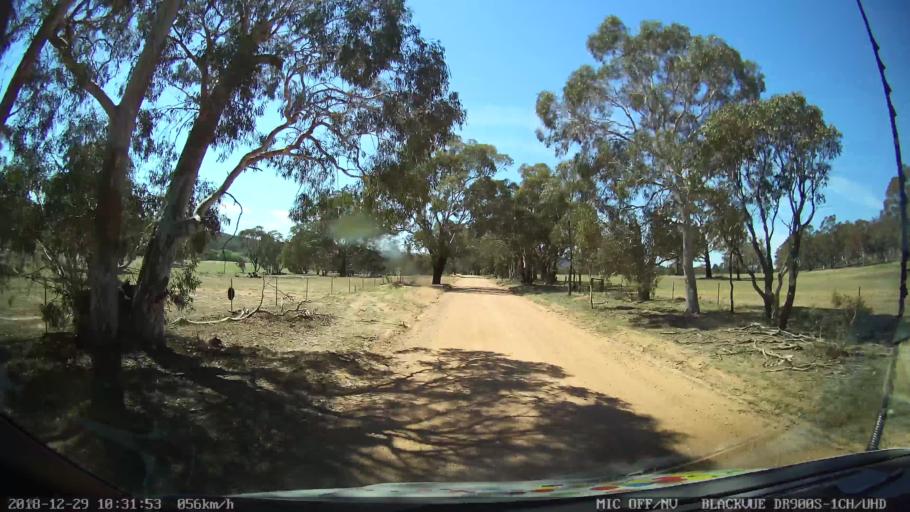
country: AU
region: New South Wales
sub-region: Yass Valley
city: Gundaroo
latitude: -34.9716
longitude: 149.4601
